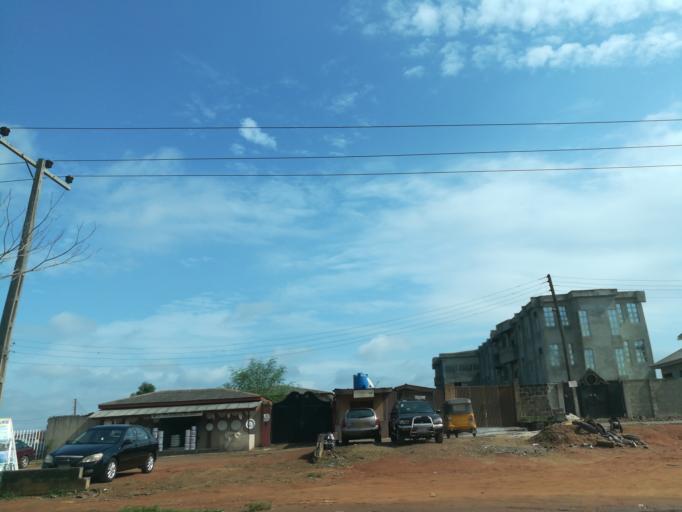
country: NG
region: Lagos
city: Ikorodu
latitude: 6.6305
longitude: 3.5192
